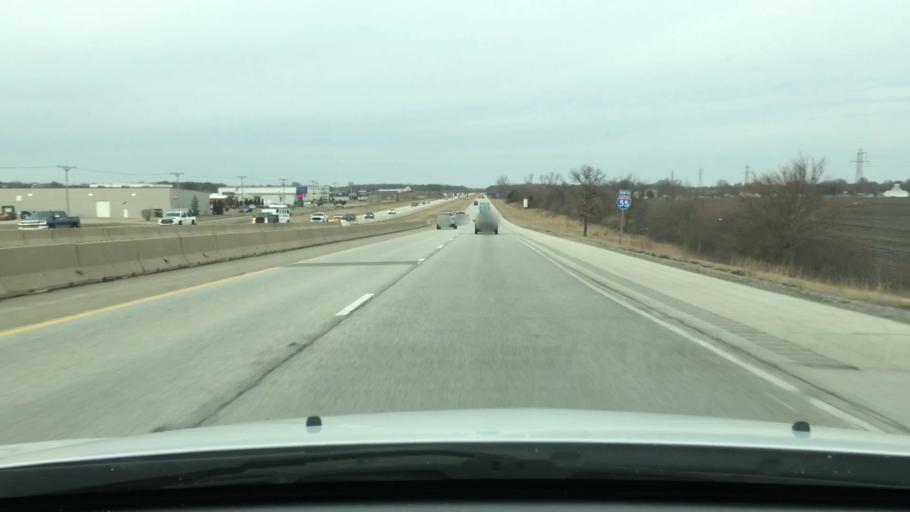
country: US
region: Illinois
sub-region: Sangamon County
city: Grandview
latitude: 39.8376
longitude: -89.5935
